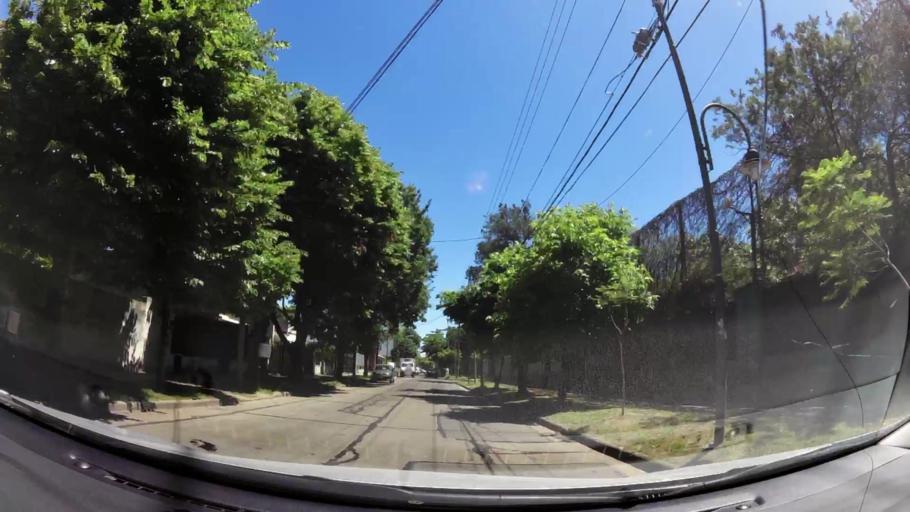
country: AR
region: Buenos Aires
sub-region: Partido de Tigre
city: Tigre
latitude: -34.4629
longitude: -58.5614
